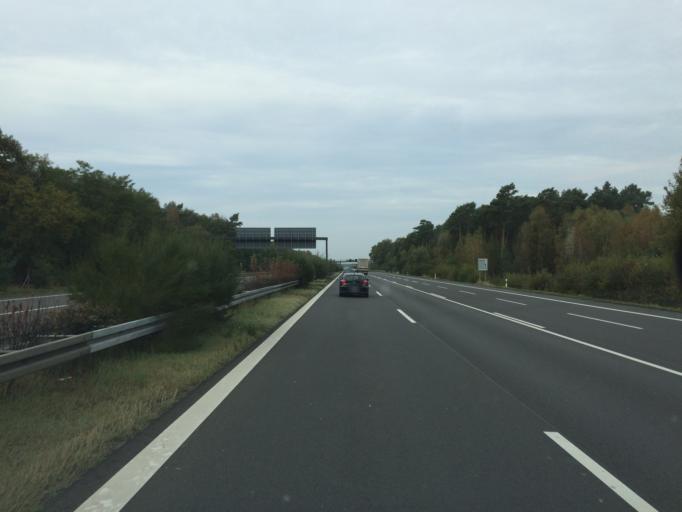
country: DE
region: Brandenburg
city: Fichtenwalde
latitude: 52.2956
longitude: 12.9057
